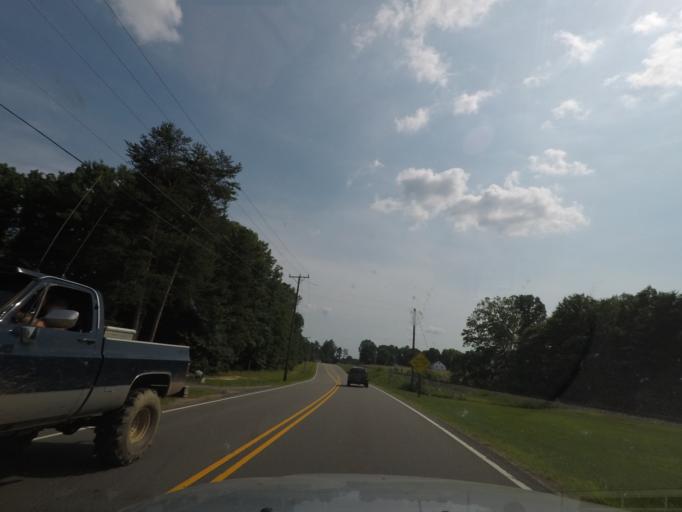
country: US
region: Virginia
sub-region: Buckingham County
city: Buckingham
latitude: 37.5508
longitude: -78.4431
